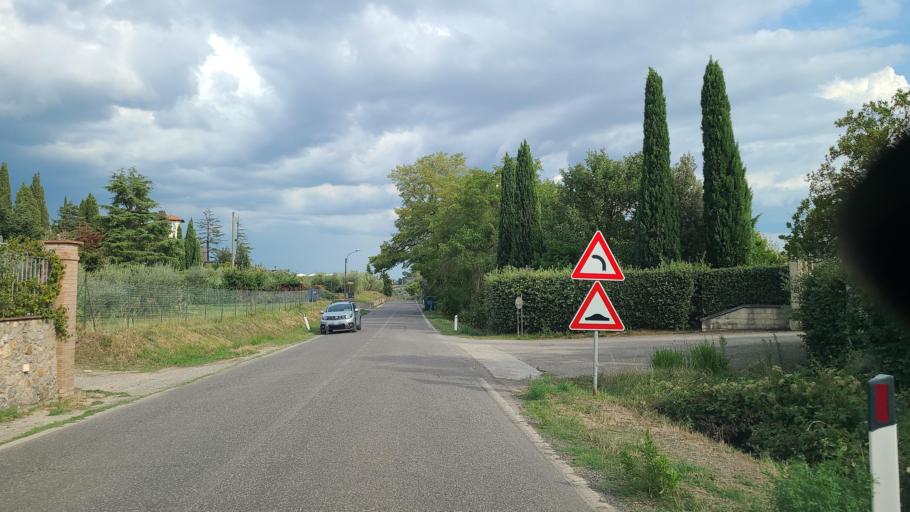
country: IT
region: Tuscany
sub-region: Provincia di Siena
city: San Gimignano
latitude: 43.4778
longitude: 11.0232
